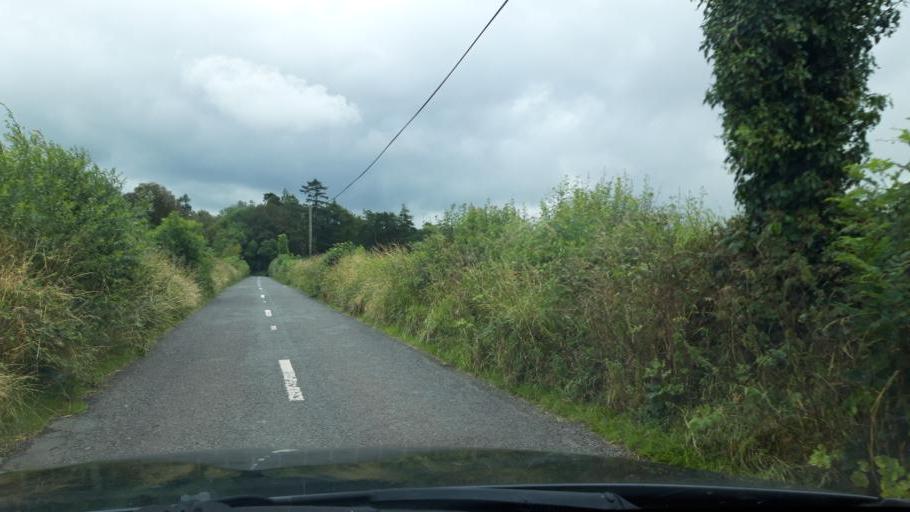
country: IE
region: Munster
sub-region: County Cork
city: Castlemartyr
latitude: 52.1322
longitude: -8.0084
